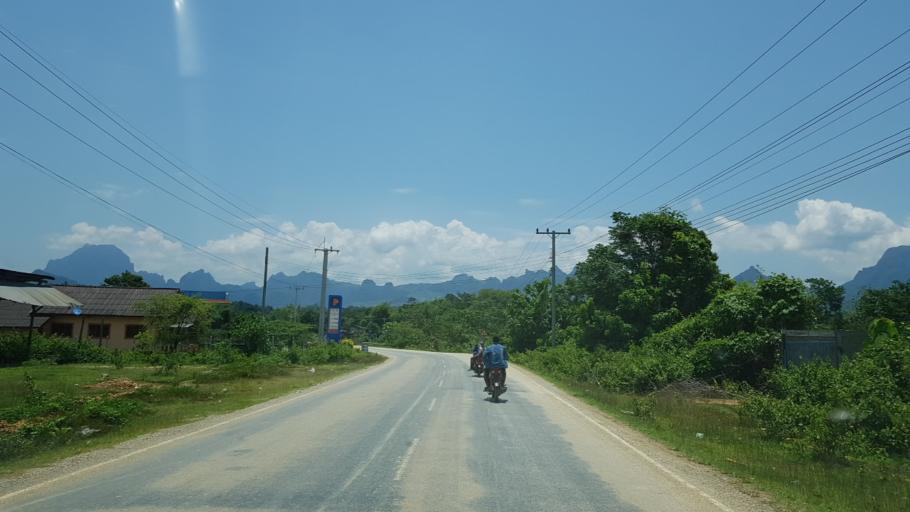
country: LA
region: Vientiane
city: Muang Kasi
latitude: 19.2527
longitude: 102.2434
